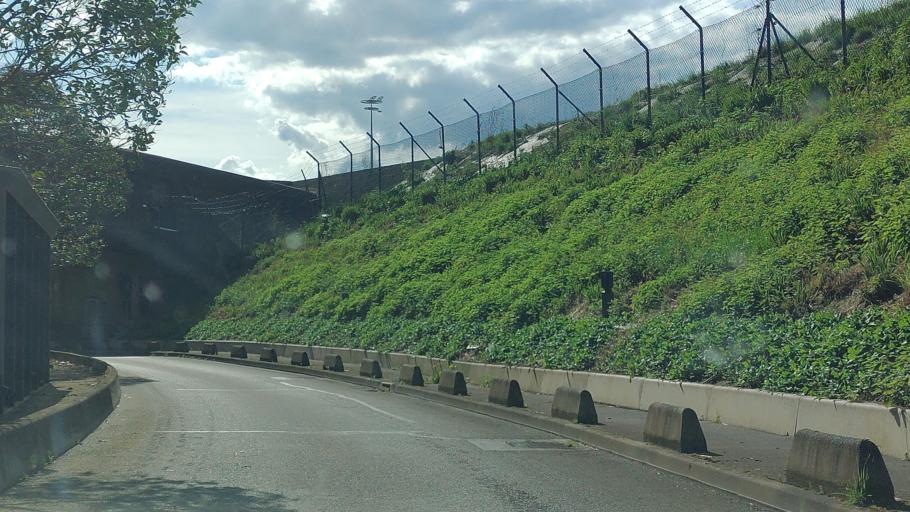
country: FR
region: Ile-de-France
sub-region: Departement du Val-d'Oise
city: Roissy-en-France
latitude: 49.0154
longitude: 2.5416
